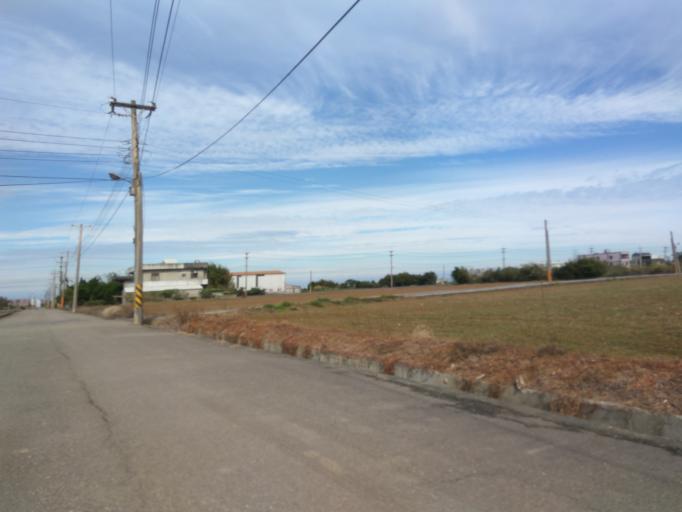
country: TW
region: Taiwan
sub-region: Hsinchu
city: Zhubei
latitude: 24.9865
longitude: 121.0884
